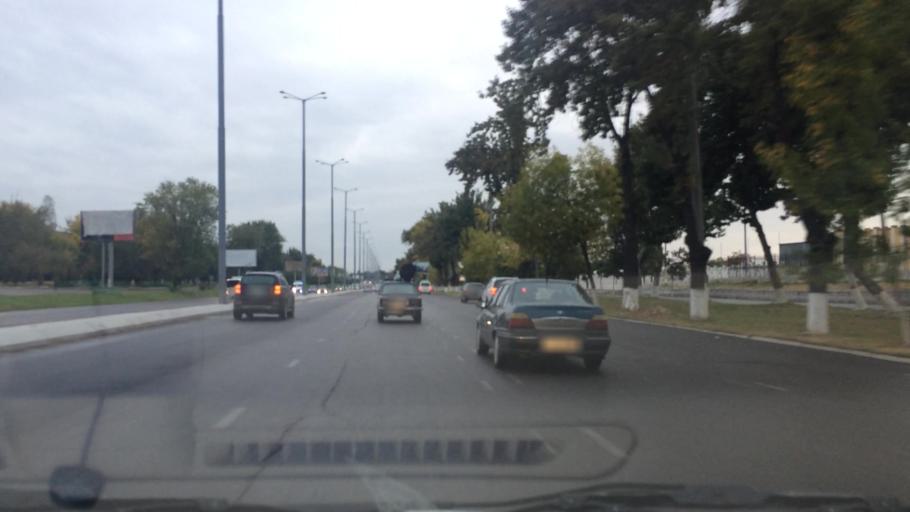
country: UZ
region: Toshkent Shahri
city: Tashkent
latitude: 41.2511
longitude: 69.1842
